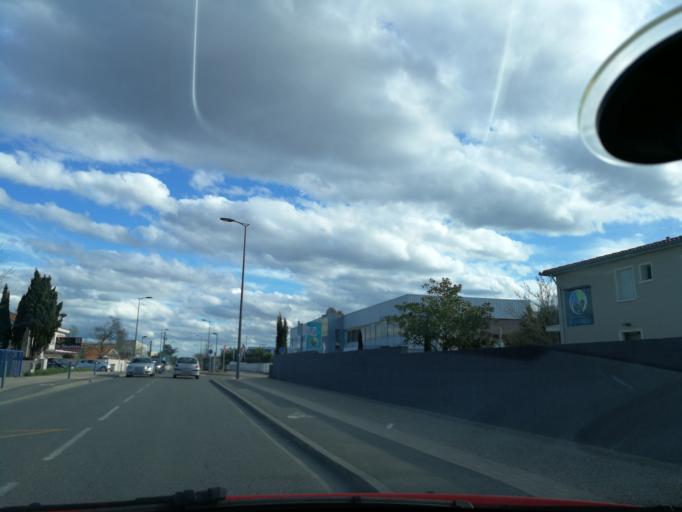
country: FR
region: Midi-Pyrenees
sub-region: Departement de la Haute-Garonne
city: Beauzelle
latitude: 43.6498
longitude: 1.3820
